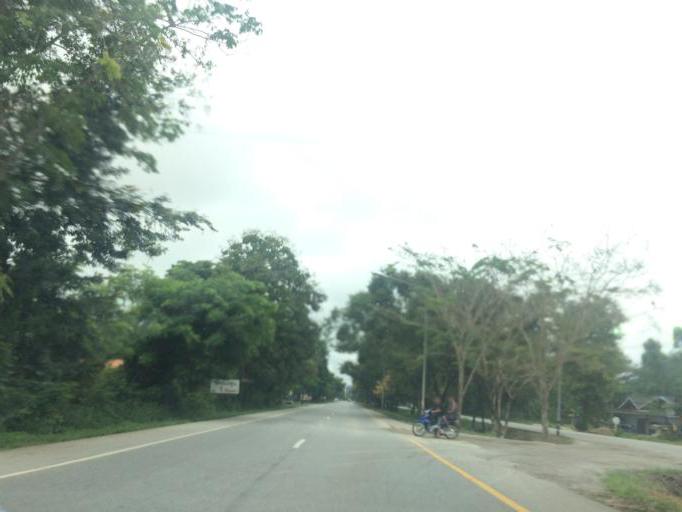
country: TH
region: Chiang Rai
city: Mae Lao
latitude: 19.8115
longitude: 99.7570
